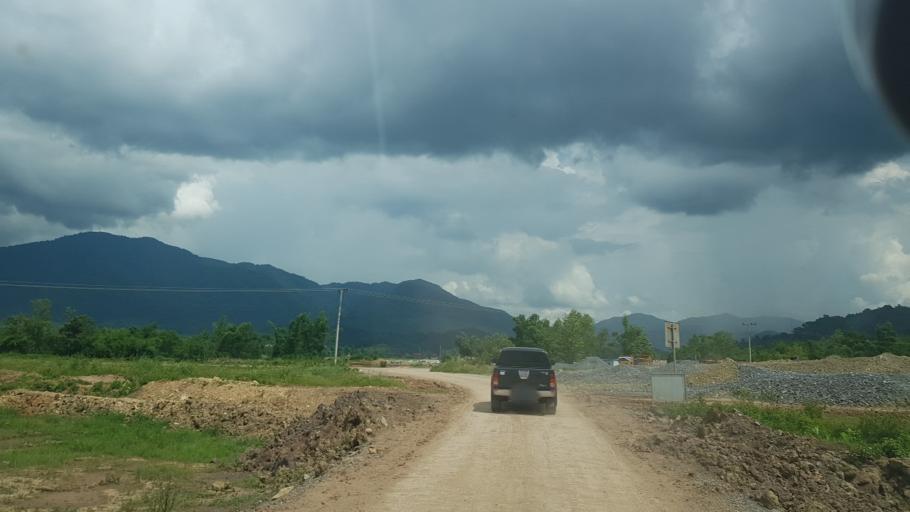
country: LA
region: Oudomxai
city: Muang Xay
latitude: 20.6783
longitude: 101.9700
